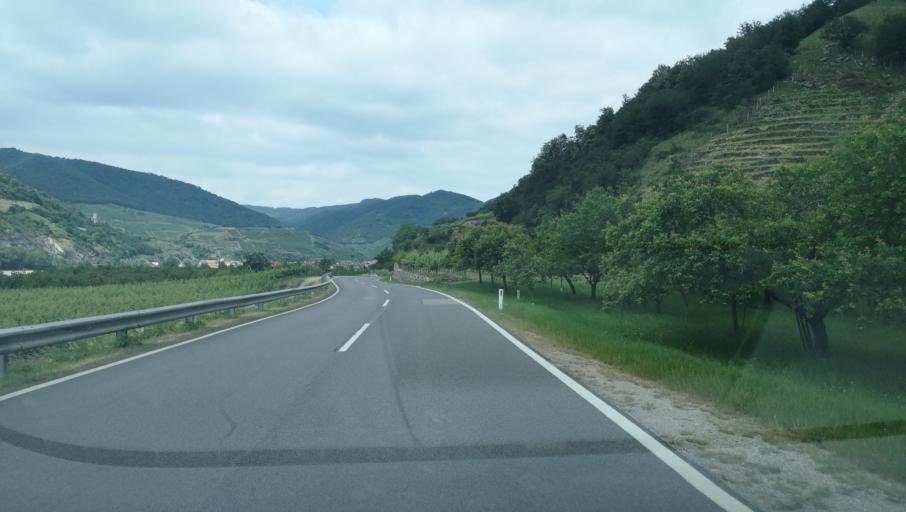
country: AT
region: Lower Austria
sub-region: Politischer Bezirk Krems
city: Spitz
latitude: 48.3444
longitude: 15.4114
